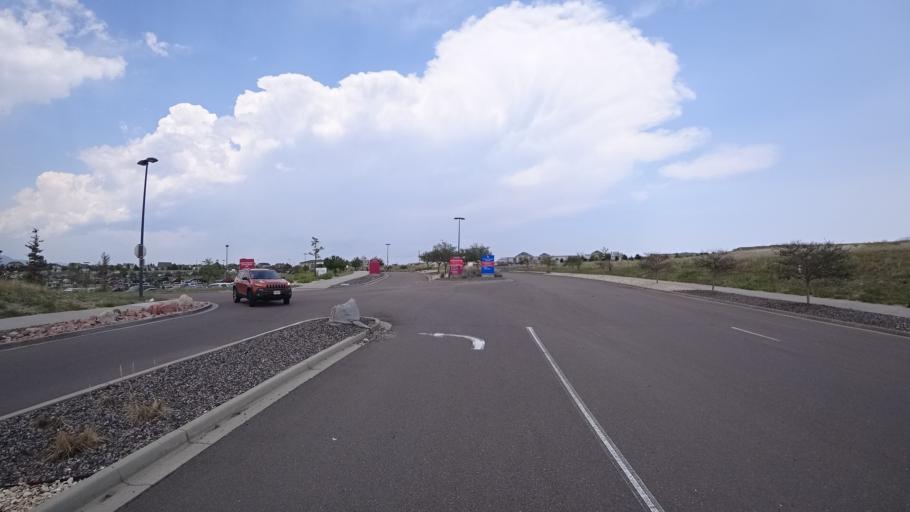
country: US
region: Colorado
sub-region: El Paso County
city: Black Forest
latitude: 38.9671
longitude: -104.7510
